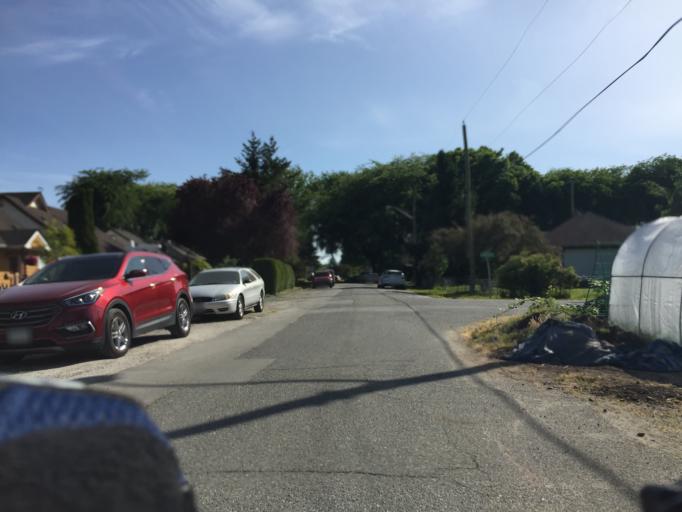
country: CA
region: British Columbia
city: Richmond
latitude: 49.1892
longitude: -123.1476
